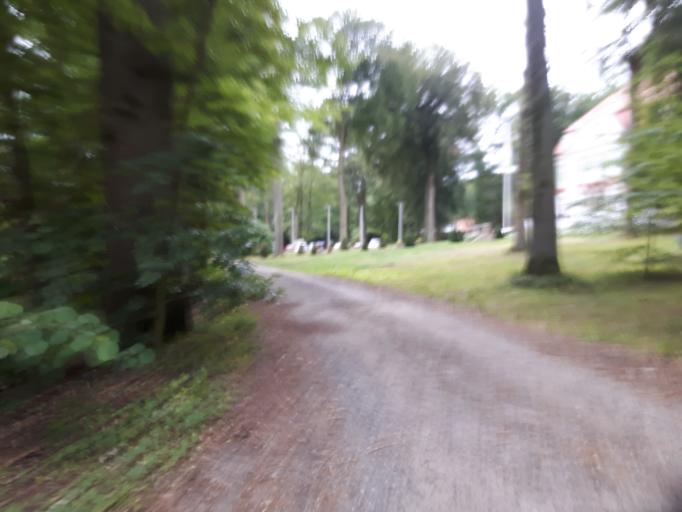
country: DE
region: Lower Saxony
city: Vierhofen
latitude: 53.2630
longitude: 10.1855
